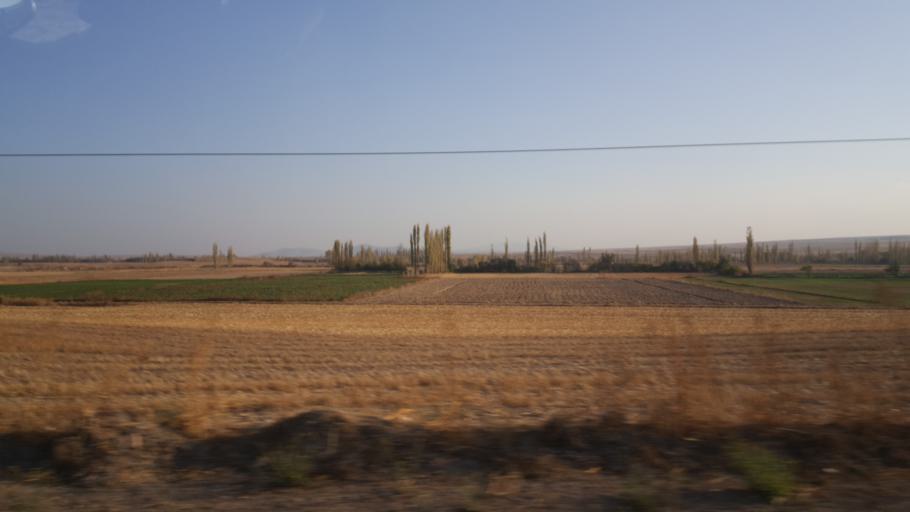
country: TR
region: Eskisehir
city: Seyitgazi
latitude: 39.4985
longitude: 30.7469
